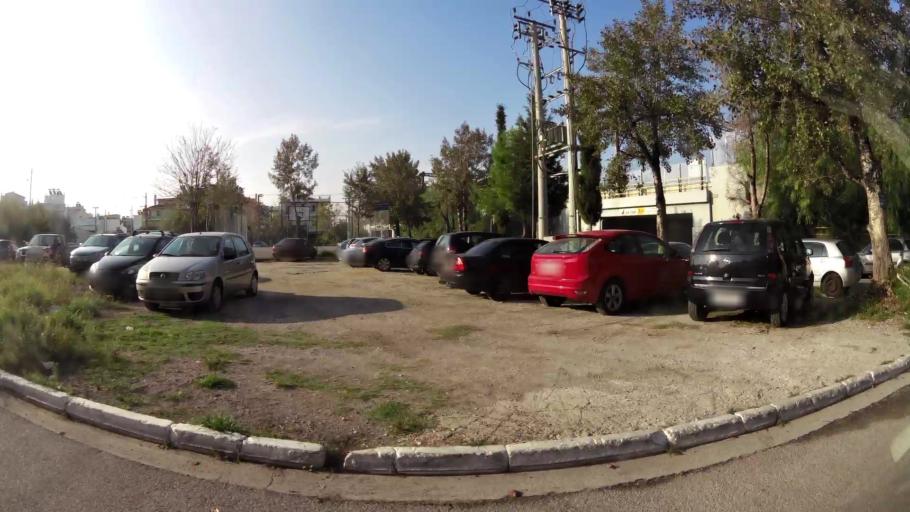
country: GR
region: Attica
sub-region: Nomarchia Dytikis Attikis
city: Zefyri
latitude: 38.0547
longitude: 23.7331
